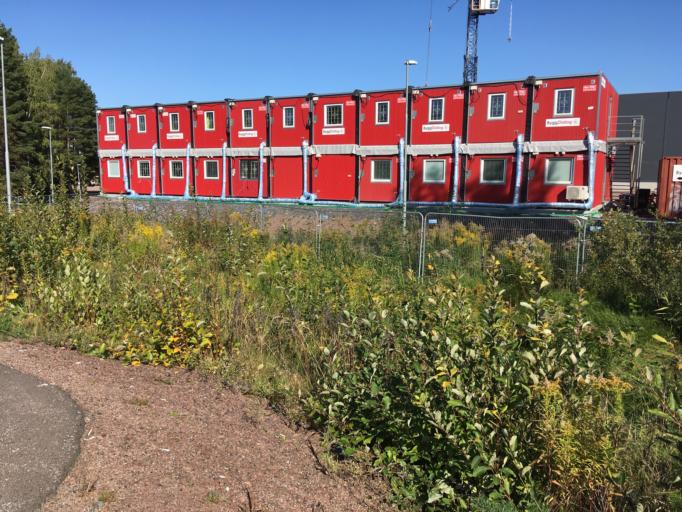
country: SE
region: Vaermland
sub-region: Karlstads Kommun
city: Karlstad
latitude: 59.3319
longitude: 13.5163
